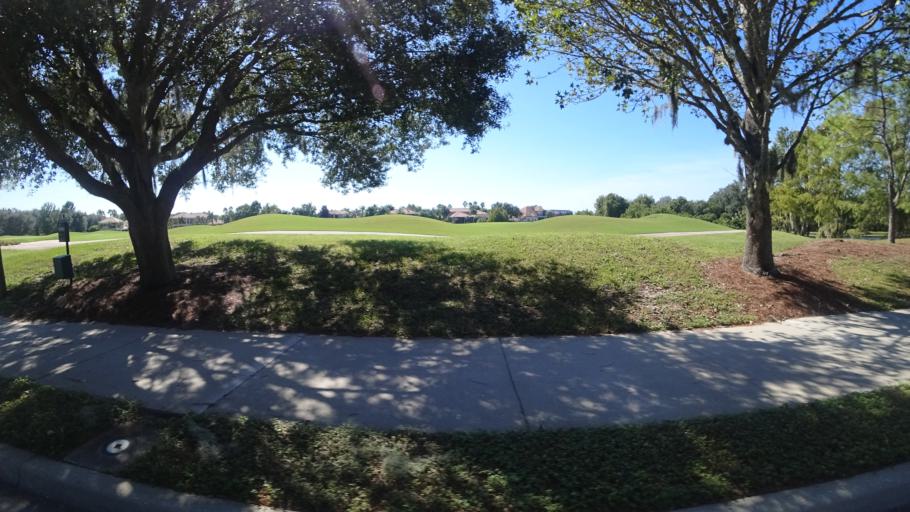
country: US
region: Florida
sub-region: Sarasota County
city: The Meadows
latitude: 27.3959
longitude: -82.4103
